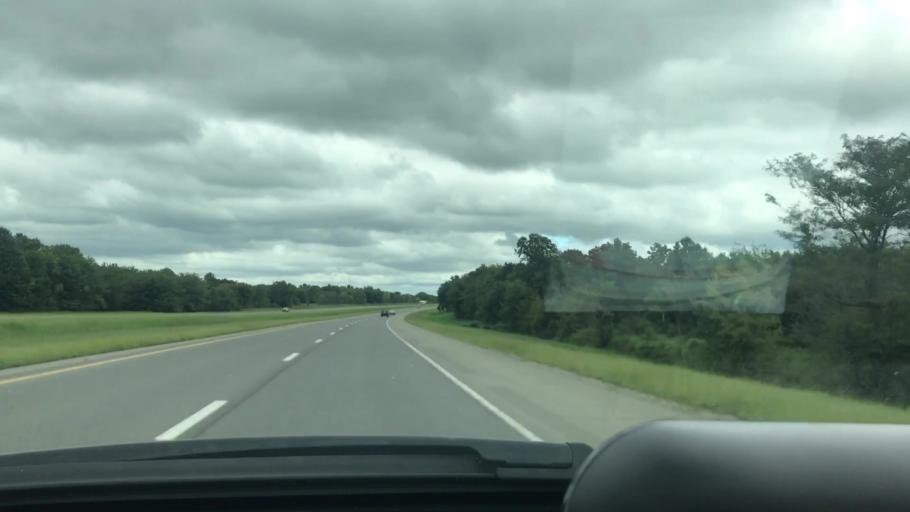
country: US
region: Oklahoma
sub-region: McIntosh County
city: Checotah
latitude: 35.5820
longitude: -95.4905
